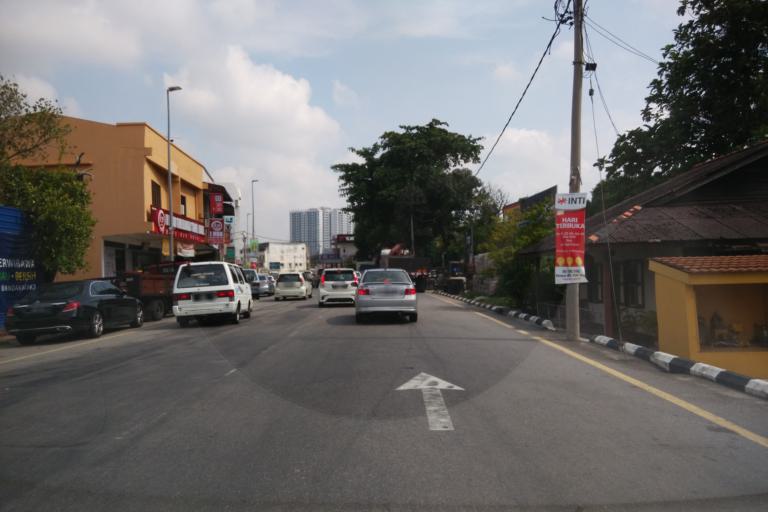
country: MY
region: Melaka
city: Malacca
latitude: 2.2088
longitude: 102.2429
